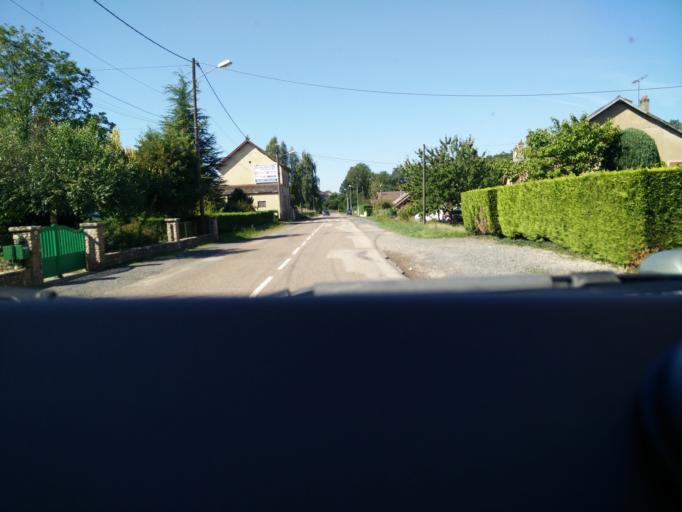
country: FR
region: Lorraine
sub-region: Departement des Vosges
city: Moyenmoutier
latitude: 48.4175
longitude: 6.8878
